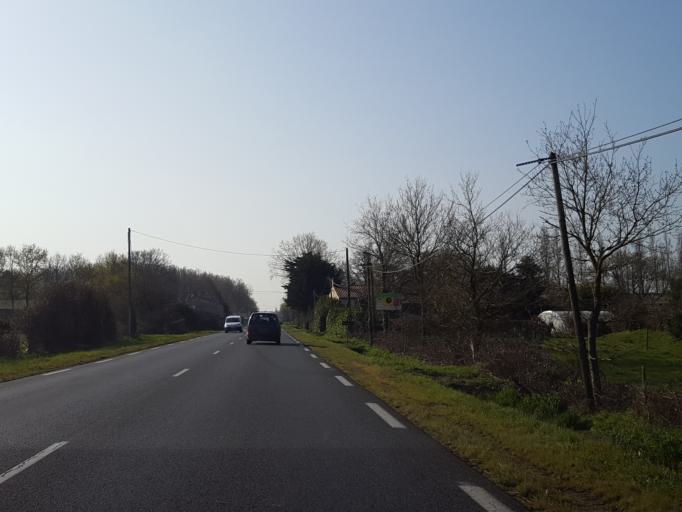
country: FR
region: Pays de la Loire
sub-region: Departement de la Loire-Atlantique
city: Geneston
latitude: 47.0749
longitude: -1.5221
